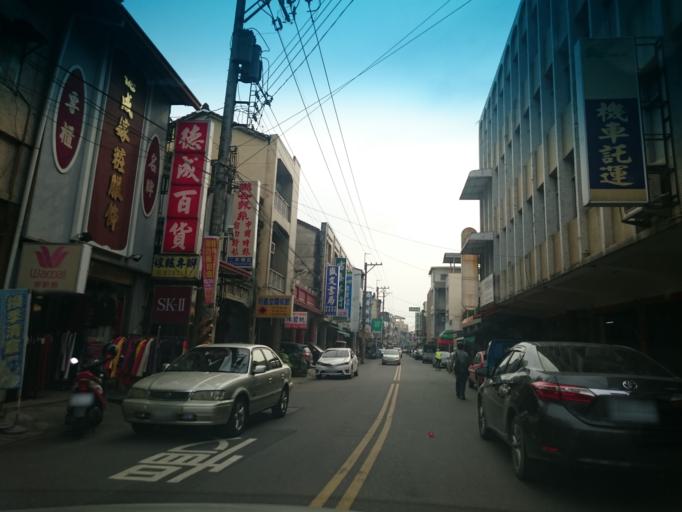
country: TW
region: Taiwan
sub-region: Nantou
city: Nantou
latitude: 23.8129
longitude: 120.6177
